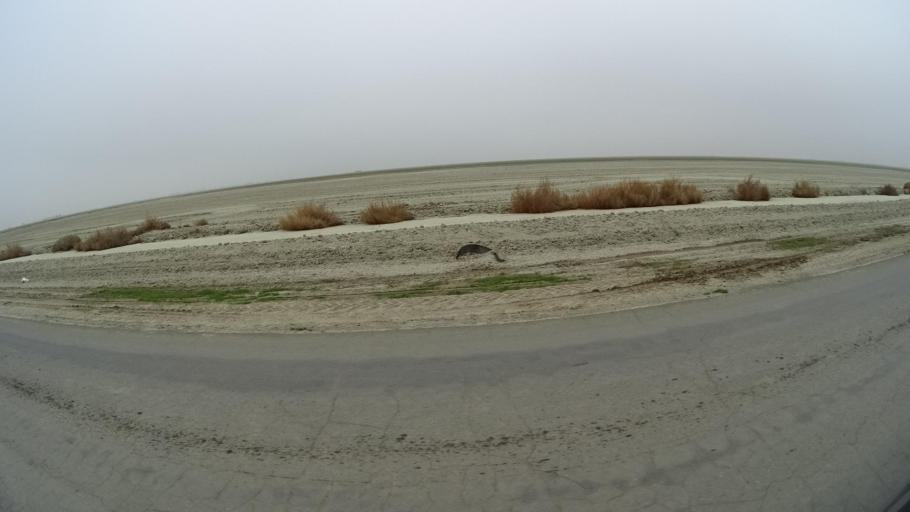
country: US
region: California
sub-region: Kern County
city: Rosedale
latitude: 35.2381
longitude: -119.2426
